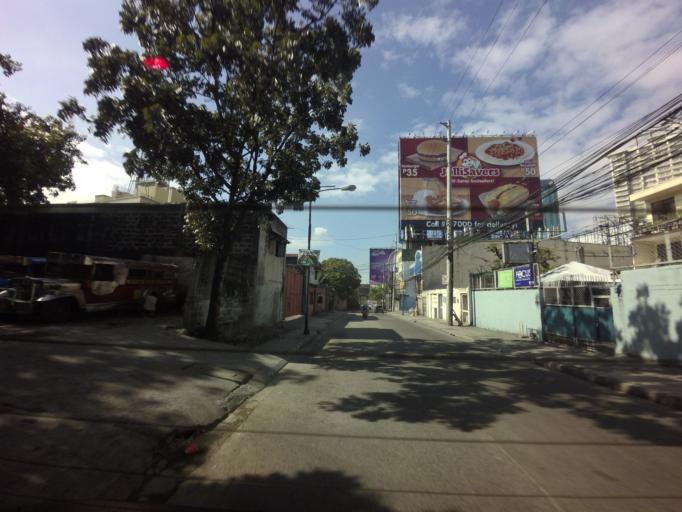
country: PH
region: Metro Manila
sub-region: Makati City
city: Makati City
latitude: 14.5630
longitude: 121.0446
